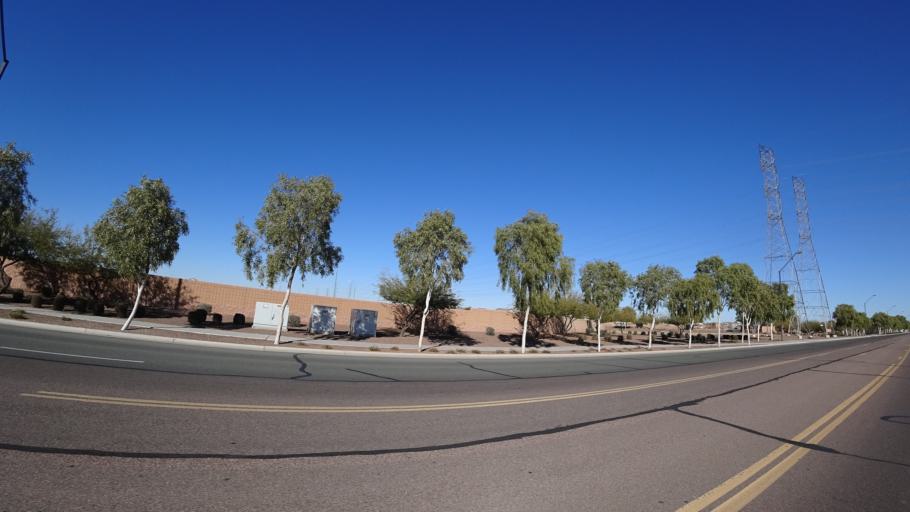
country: US
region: Arizona
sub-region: Maricopa County
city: Avondale
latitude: 33.4205
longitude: -112.3202
